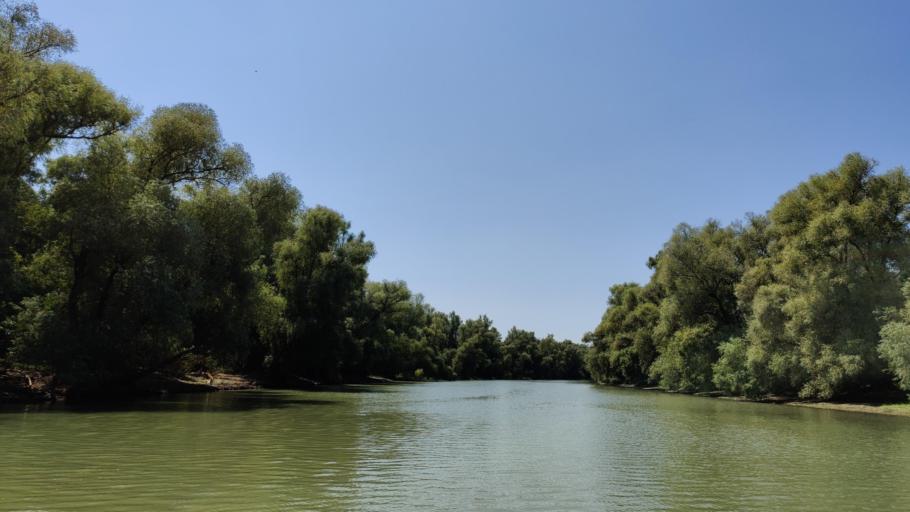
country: RO
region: Tulcea
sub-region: Comuna Nufaru
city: Nufaru
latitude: 45.2339
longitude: 28.9126
